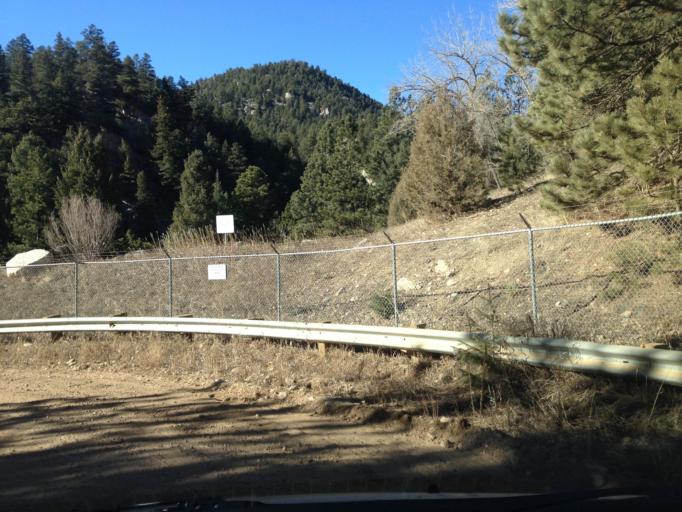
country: US
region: Colorado
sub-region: Boulder County
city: Coal Creek
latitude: 39.9398
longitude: -105.3502
